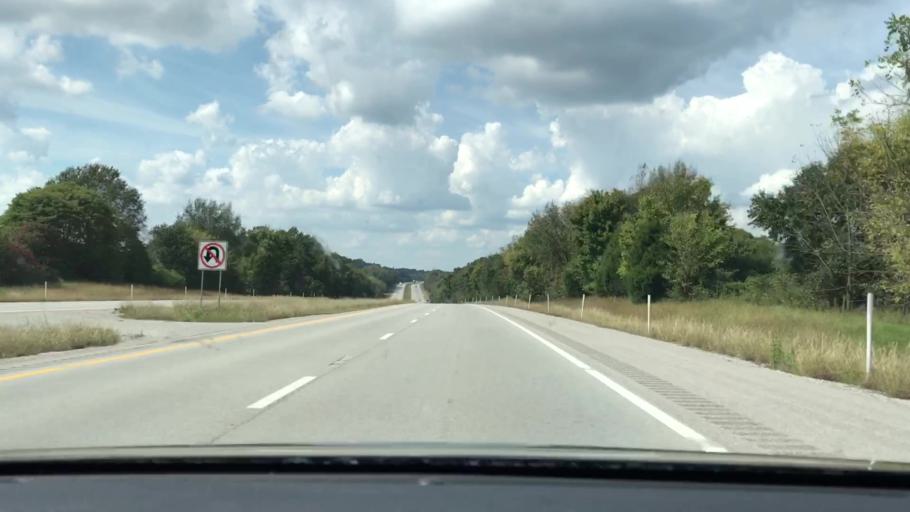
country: US
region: Kentucky
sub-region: Barren County
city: Glasgow
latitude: 37.0071
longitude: -86.0093
